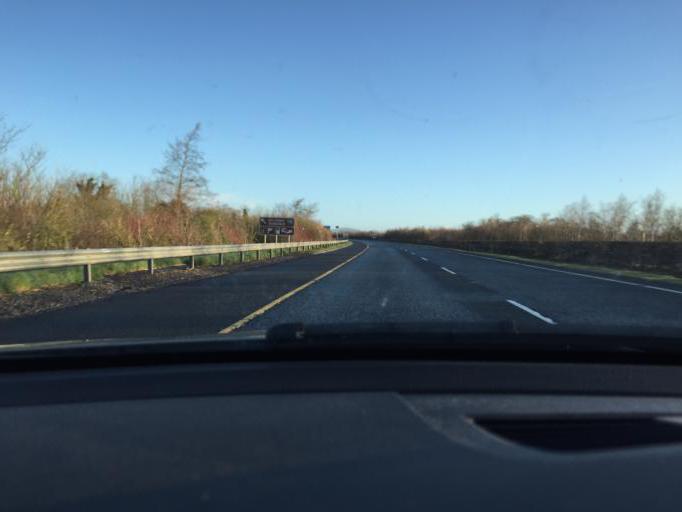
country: IE
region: Leinster
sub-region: Lu
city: Dromiskin
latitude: 53.9560
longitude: -6.4193
